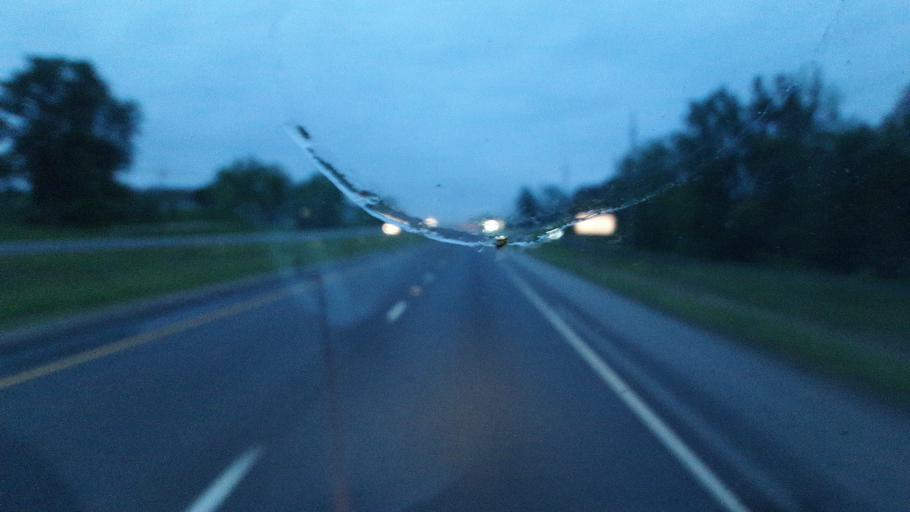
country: US
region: Indiana
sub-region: Steuben County
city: Angola
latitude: 41.6240
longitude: -85.0482
